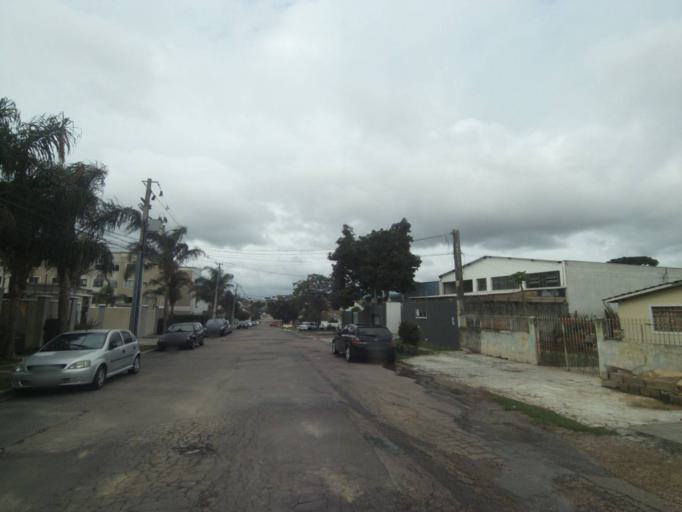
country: BR
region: Parana
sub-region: Curitiba
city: Curitiba
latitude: -25.4888
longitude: -49.3128
